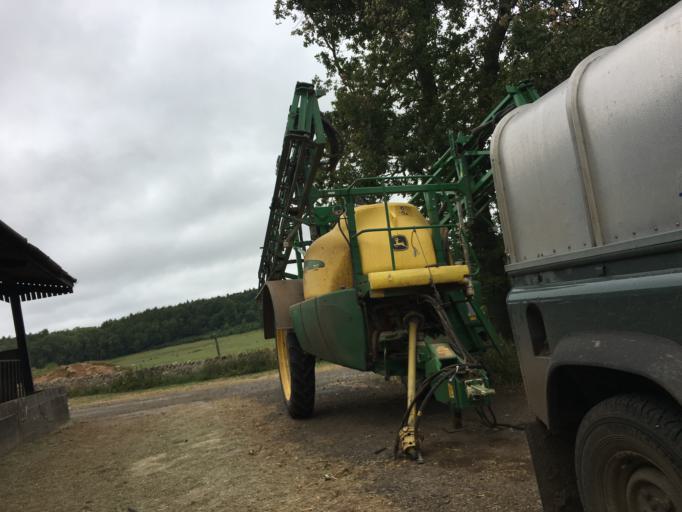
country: GB
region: England
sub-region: Northumberland
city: Belford
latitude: 55.6089
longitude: -1.8683
